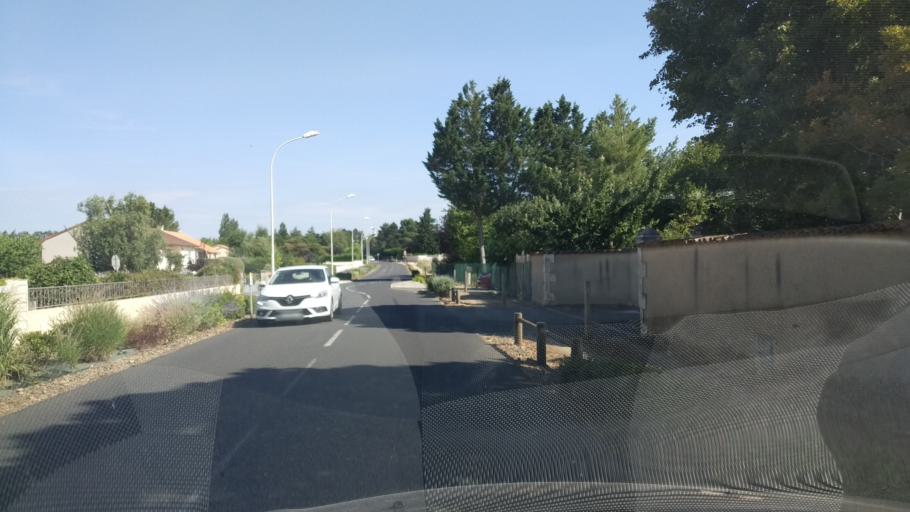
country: FR
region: Poitou-Charentes
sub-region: Departement de la Vienne
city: Cisse
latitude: 46.6389
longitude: 0.2403
